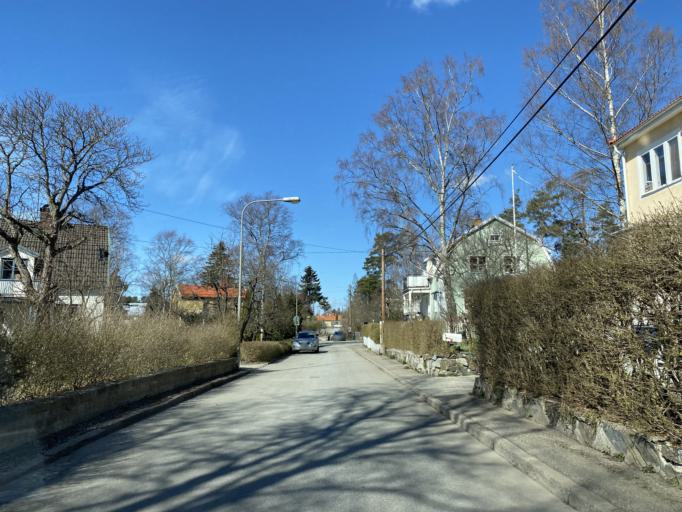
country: SE
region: Stockholm
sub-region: Stockholms Kommun
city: Arsta
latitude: 59.2750
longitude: 18.0631
